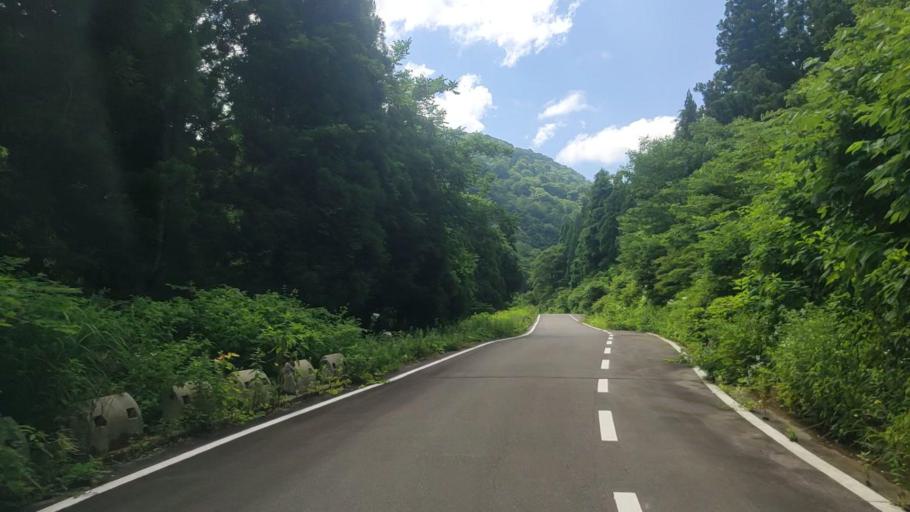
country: JP
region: Fukui
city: Katsuyama
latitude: 36.1634
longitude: 136.5252
